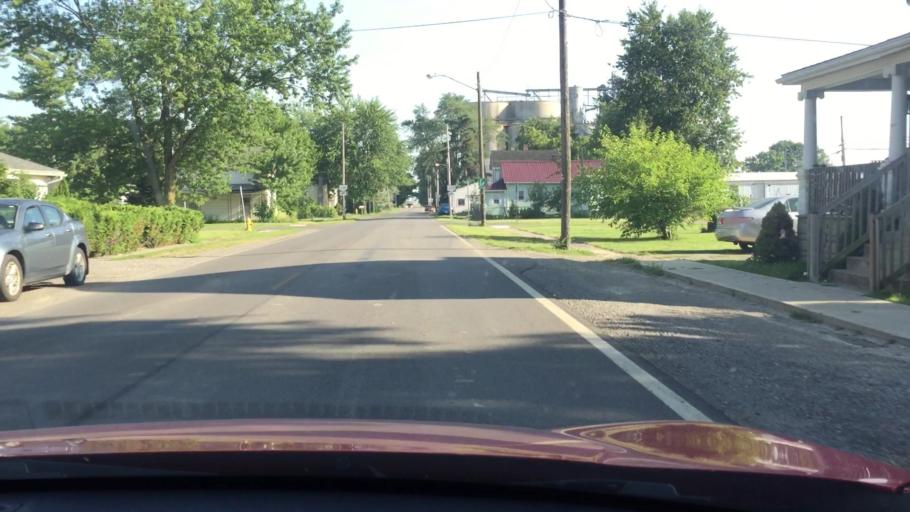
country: US
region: Ohio
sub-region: Hardin County
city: Ada
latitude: 40.7075
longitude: -83.8422
